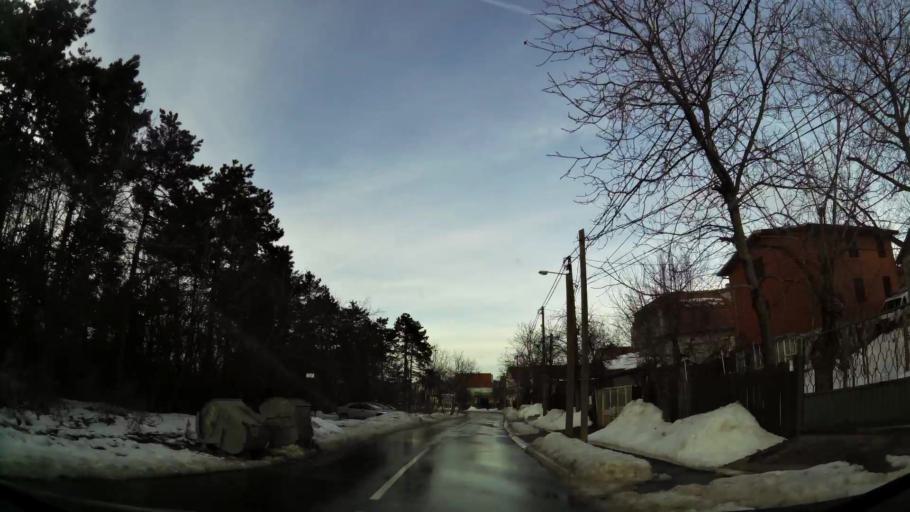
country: RS
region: Central Serbia
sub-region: Belgrade
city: Zvezdara
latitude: 44.7336
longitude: 20.5108
